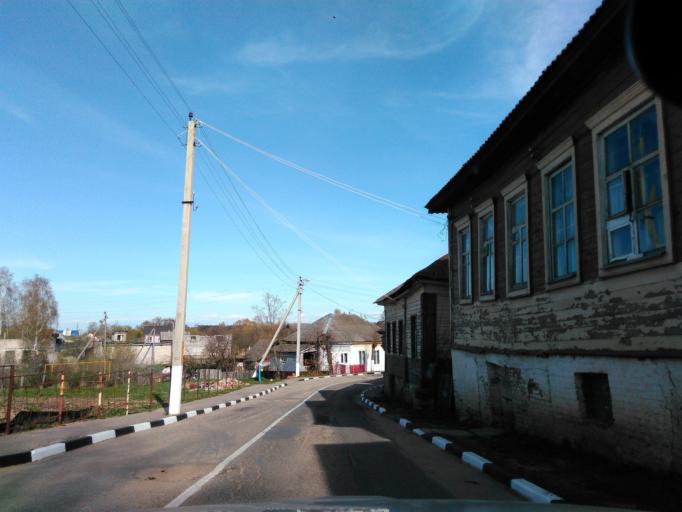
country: BY
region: Vitebsk
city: Chashniki
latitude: 54.8630
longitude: 29.1622
